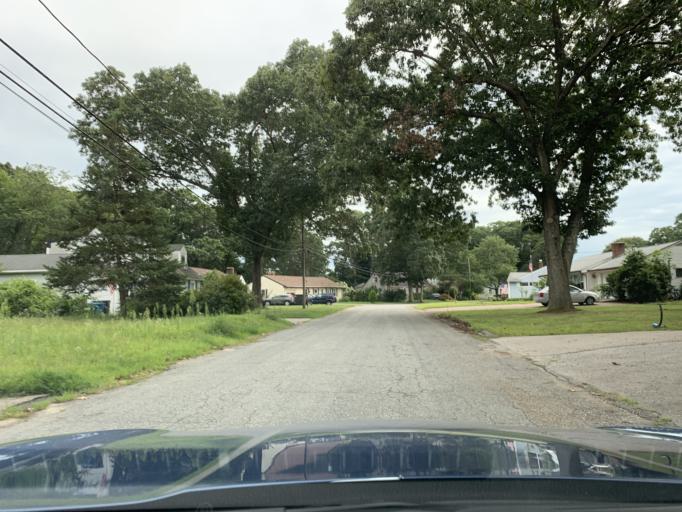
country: US
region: Rhode Island
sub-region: Kent County
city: East Greenwich
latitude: 41.6159
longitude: -71.4660
